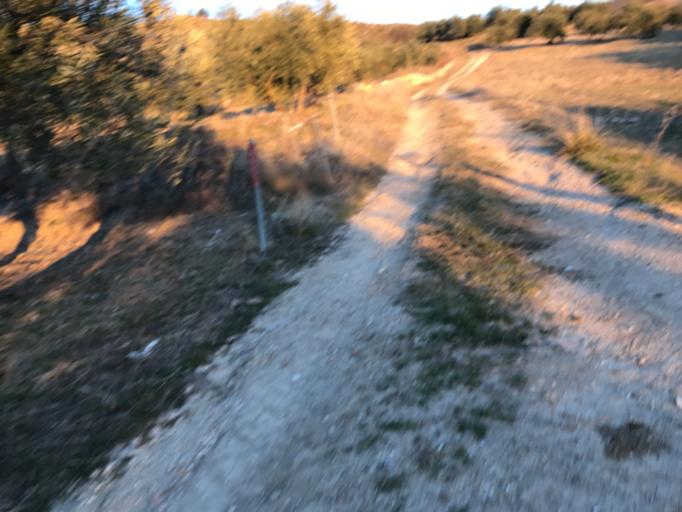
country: ES
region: Andalusia
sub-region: Provincia de Granada
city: Beas de Granada
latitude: 37.2225
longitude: -3.4717
